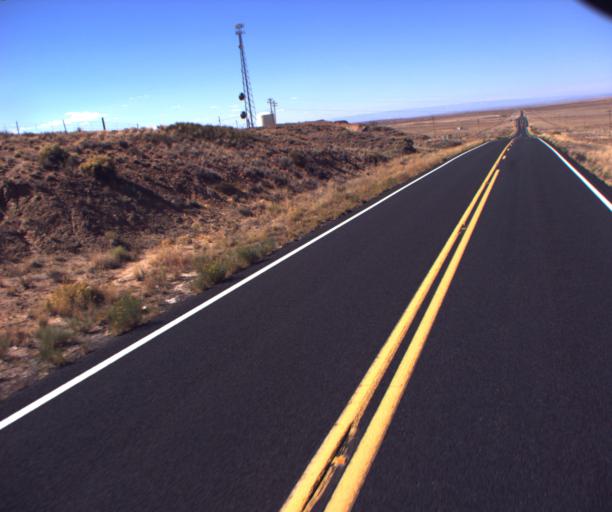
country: US
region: Arizona
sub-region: Coconino County
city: Tuba City
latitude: 35.9937
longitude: -111.0198
